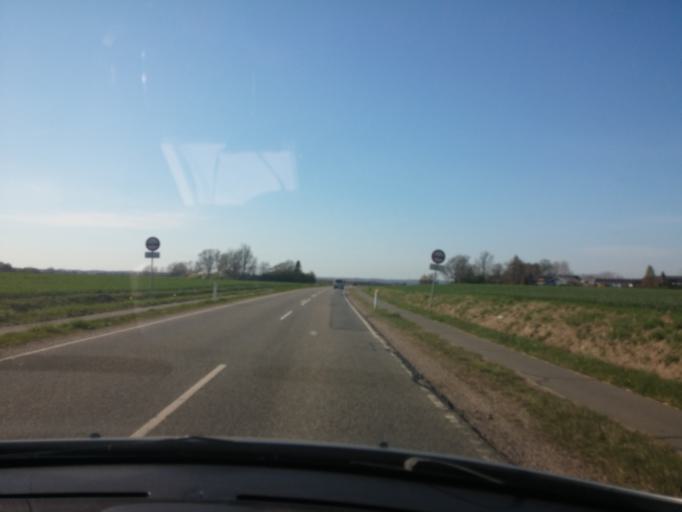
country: DK
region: Central Jutland
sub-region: Odder Kommune
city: Odder
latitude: 55.9387
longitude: 10.2150
